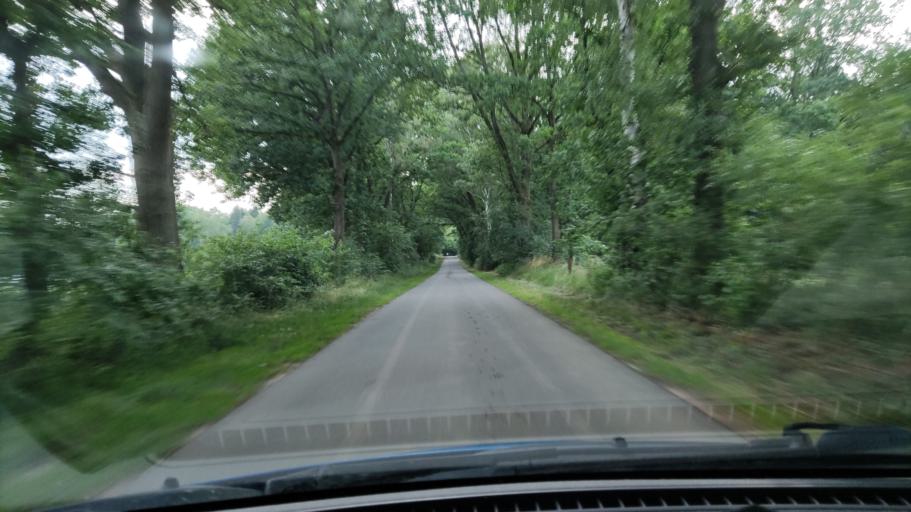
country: DE
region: Lower Saxony
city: Amelinghausen
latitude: 53.1337
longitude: 10.2383
